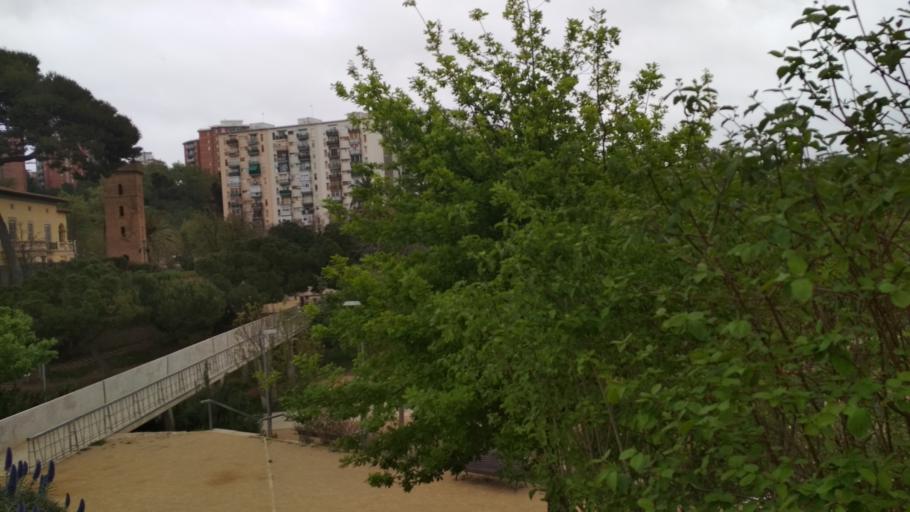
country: ES
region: Catalonia
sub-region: Provincia de Barcelona
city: L'Hospitalet de Llobregat
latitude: 41.3640
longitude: 2.0955
